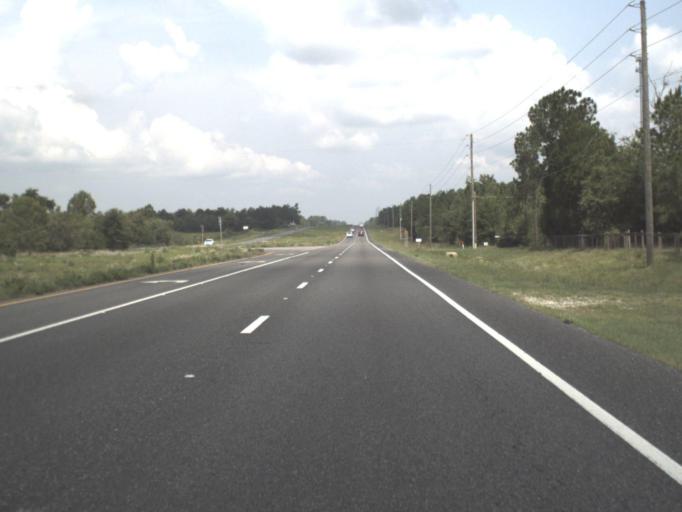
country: US
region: Florida
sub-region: Levy County
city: East Bronson
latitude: 29.4145
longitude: -82.5517
